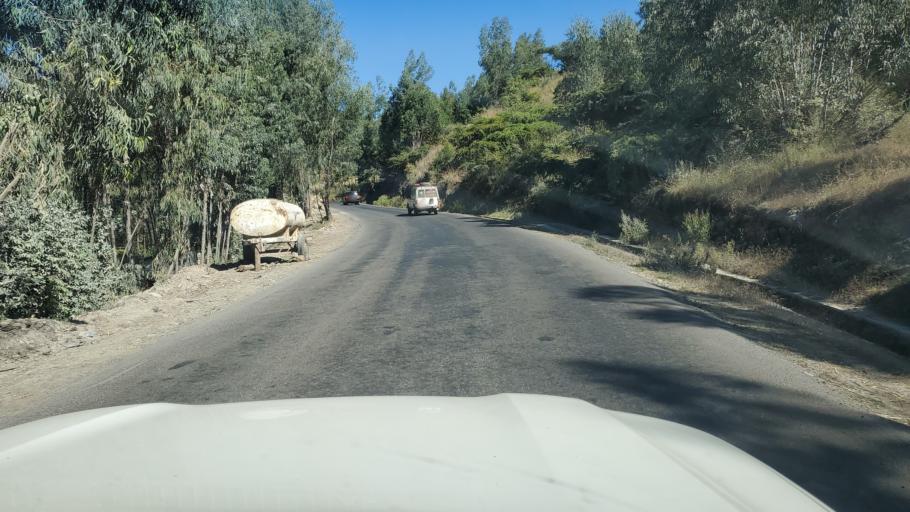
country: ET
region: Amhara
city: Dese
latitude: 11.0935
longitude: 39.6329
